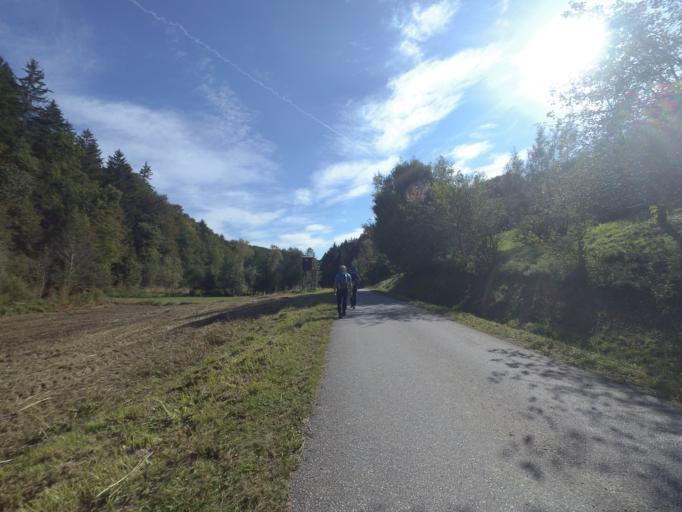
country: AT
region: Styria
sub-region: Politischer Bezirk Leibnitz
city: Kitzeck im Sausal
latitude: 46.7726
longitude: 15.4411
